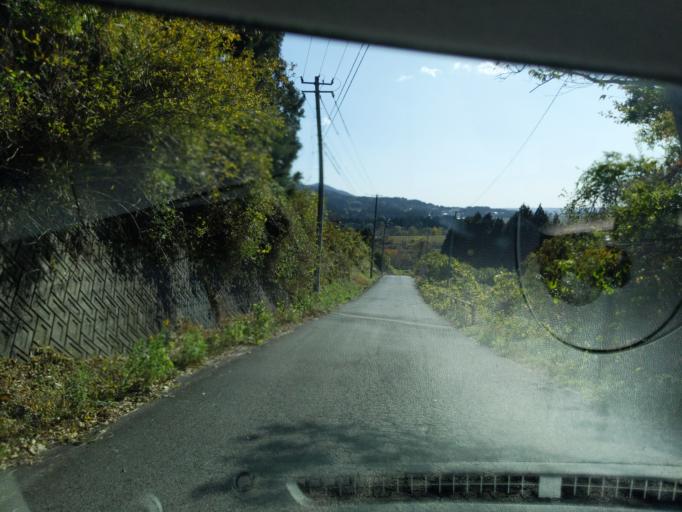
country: JP
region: Iwate
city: Ichinoseki
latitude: 39.0231
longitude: 141.1251
